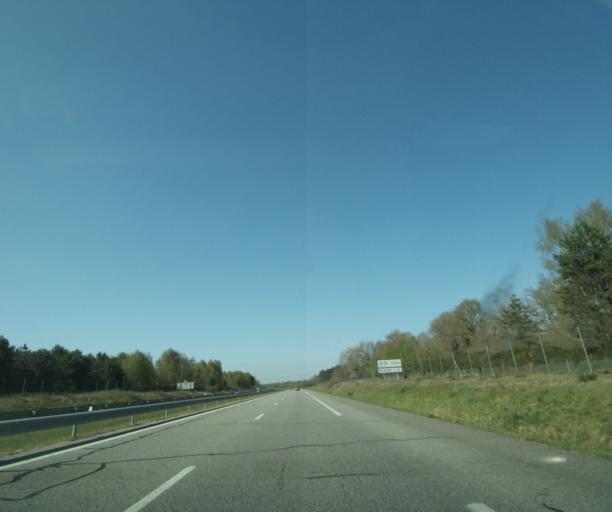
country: FR
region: Centre
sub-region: Departement du Loiret
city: Nogent-sur-Vernisson
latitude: 47.7575
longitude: 2.7193
